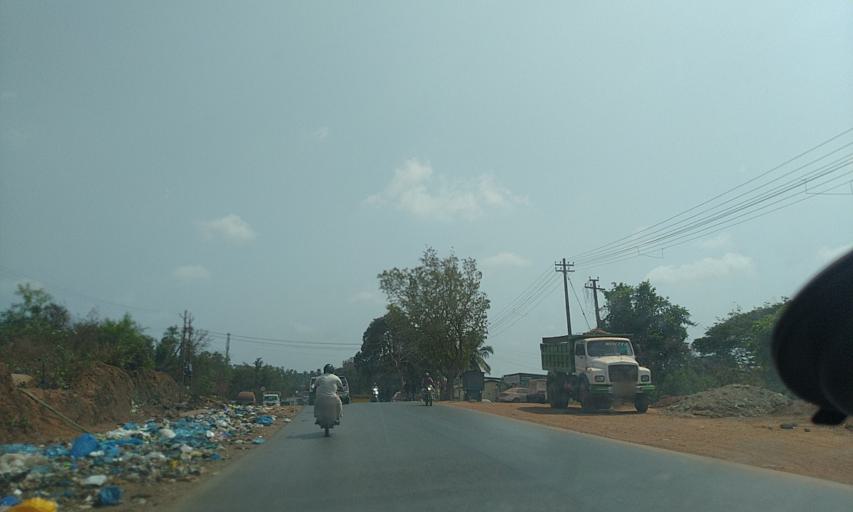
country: IN
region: Goa
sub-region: North Goa
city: Colovale
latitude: 15.6183
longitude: 73.8227
